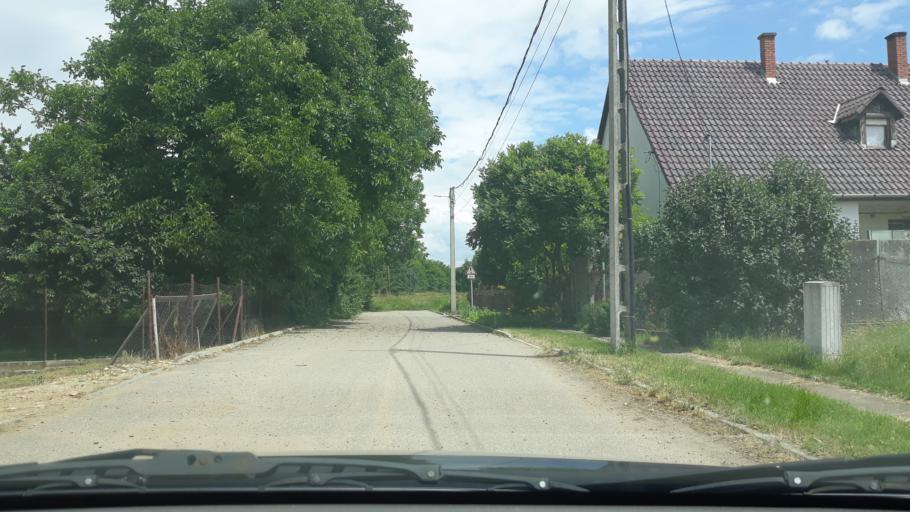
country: HU
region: Hajdu-Bihar
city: Biharkeresztes
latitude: 47.1330
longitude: 21.7334
